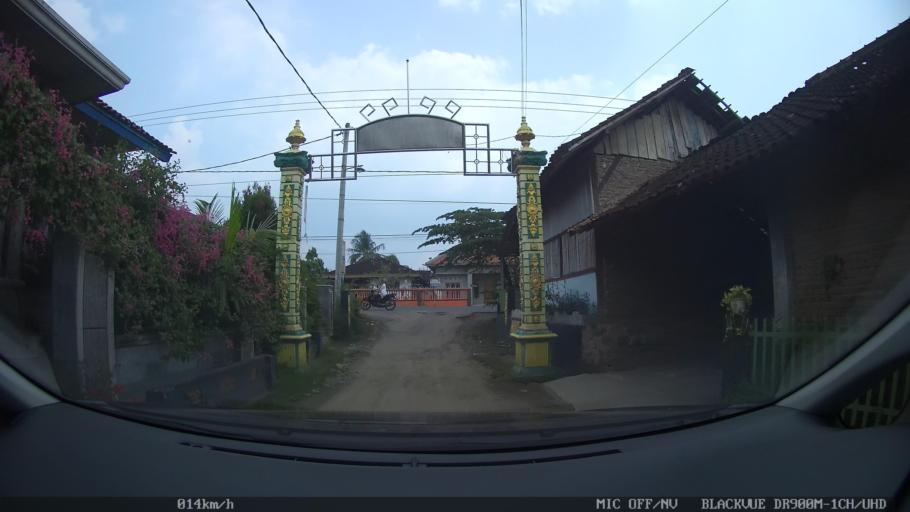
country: ID
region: Lampung
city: Gadingrejo
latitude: -5.3739
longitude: 105.0699
